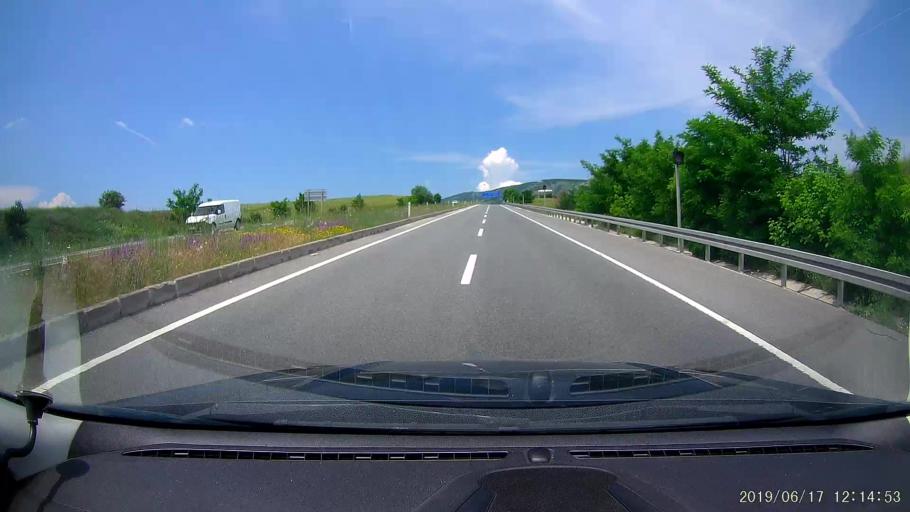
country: TR
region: Karabuk
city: Gozyeri
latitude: 40.8695
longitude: 32.5885
